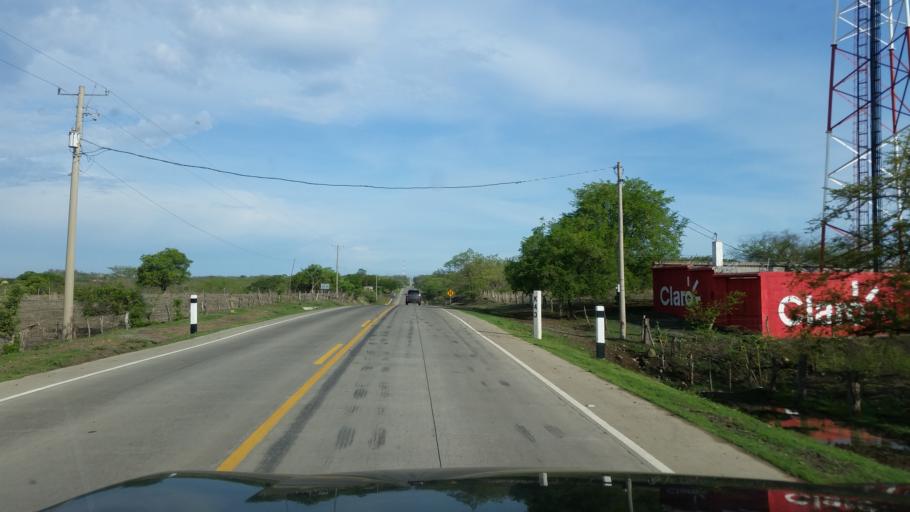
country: NI
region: Leon
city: Nagarote
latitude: 12.1112
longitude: -86.6003
